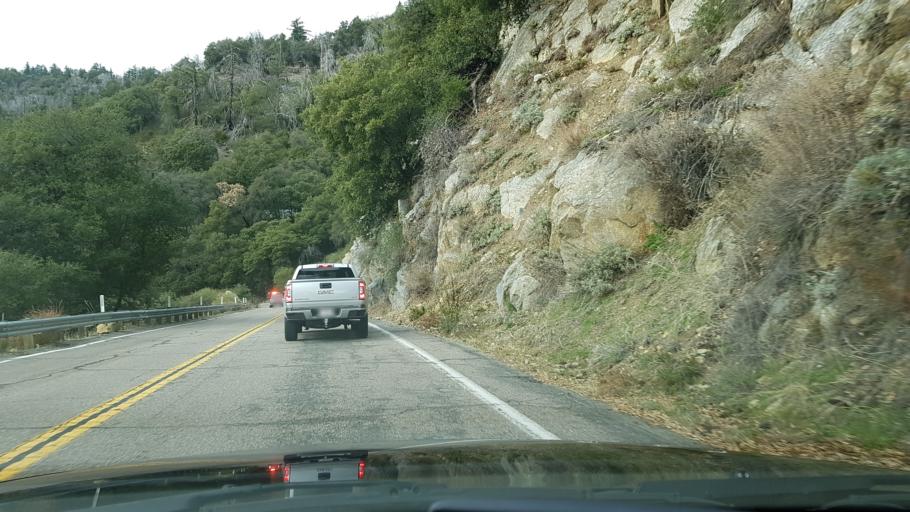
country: US
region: California
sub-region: Riverside County
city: Aguanga
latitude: 33.3037
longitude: -116.8739
